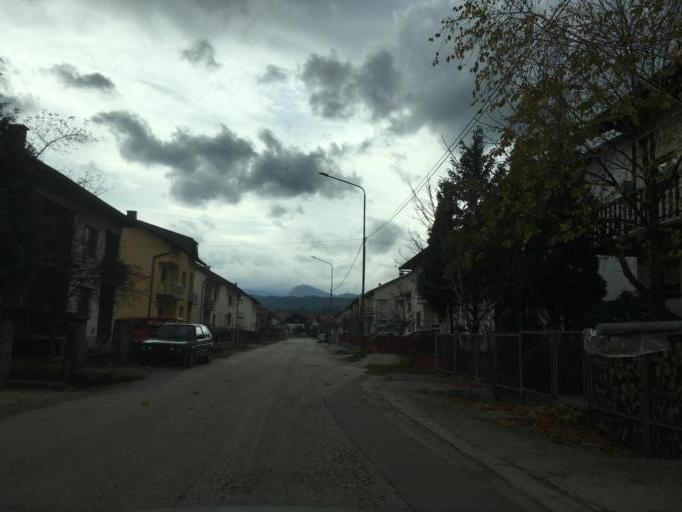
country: BA
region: Federation of Bosnia and Herzegovina
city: Bugojno
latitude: 44.0630
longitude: 17.4539
